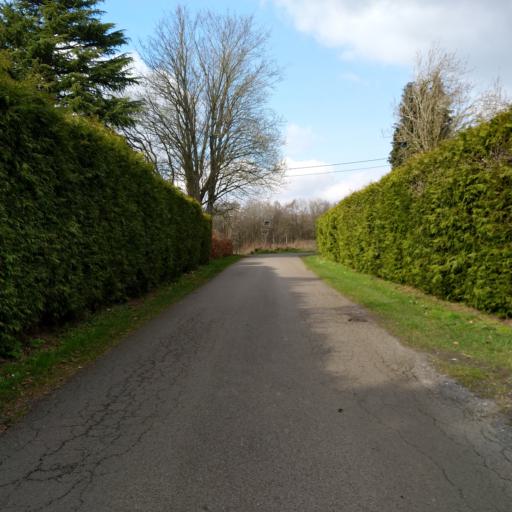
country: BE
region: Wallonia
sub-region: Province du Hainaut
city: Mons
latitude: 50.5113
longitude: 3.9688
